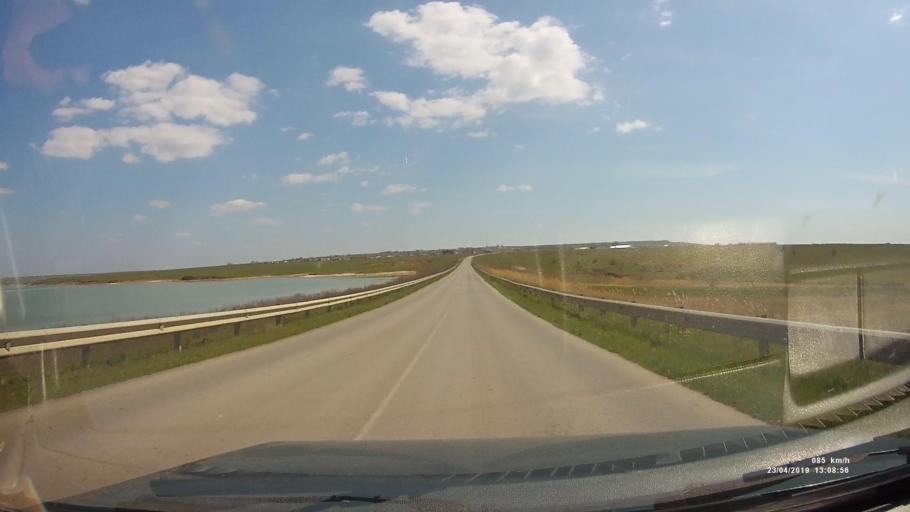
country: RU
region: Kalmykiya
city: Yashalta
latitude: 46.5795
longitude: 42.7821
